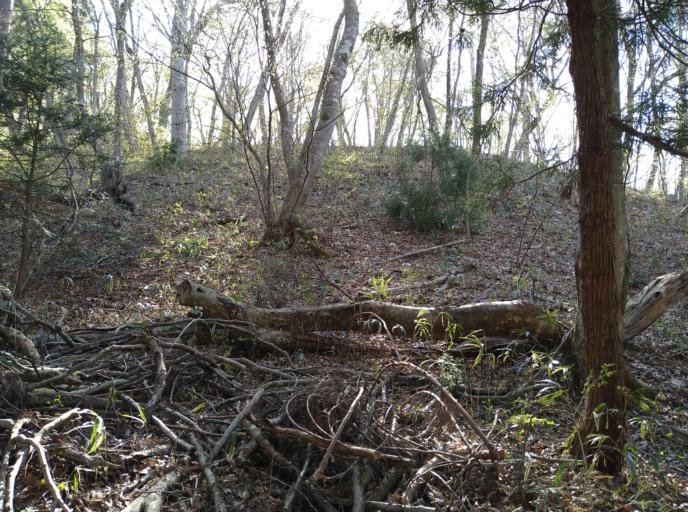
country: JP
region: Iwate
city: Ichinoseki
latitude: 38.8867
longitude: 141.0027
